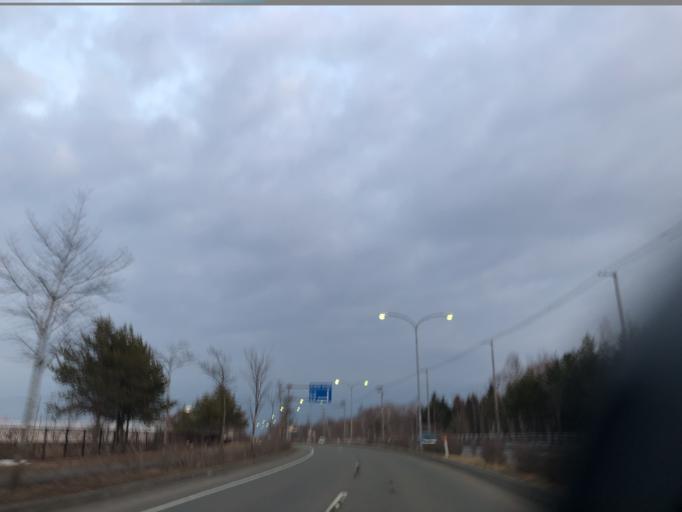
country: JP
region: Hokkaido
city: Chitose
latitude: 42.8218
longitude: 141.6724
